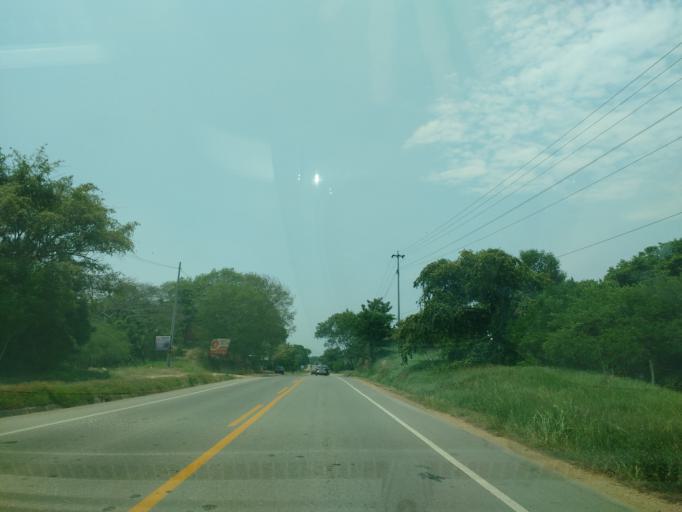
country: CO
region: Cundinamarca
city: Ricaurte
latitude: 4.2579
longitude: -74.7469
